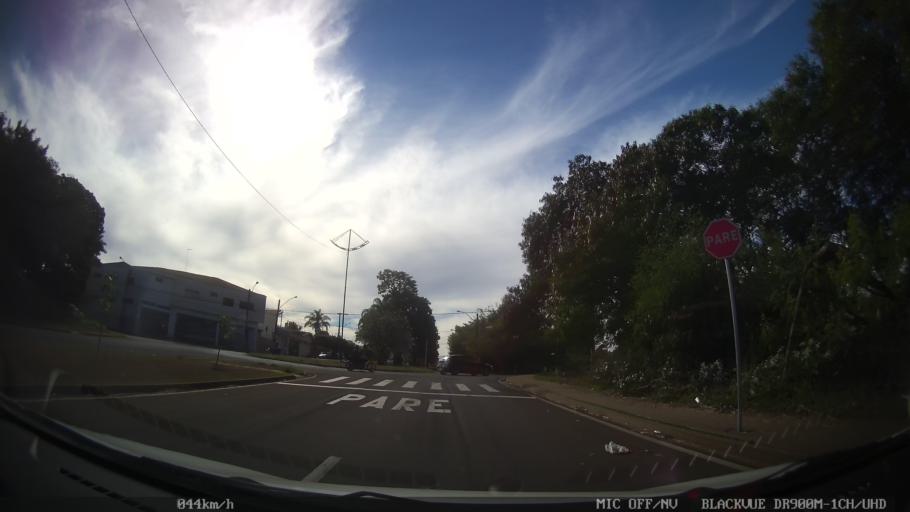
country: BR
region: Sao Paulo
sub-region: Catanduva
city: Catanduva
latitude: -21.1203
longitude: -48.9729
